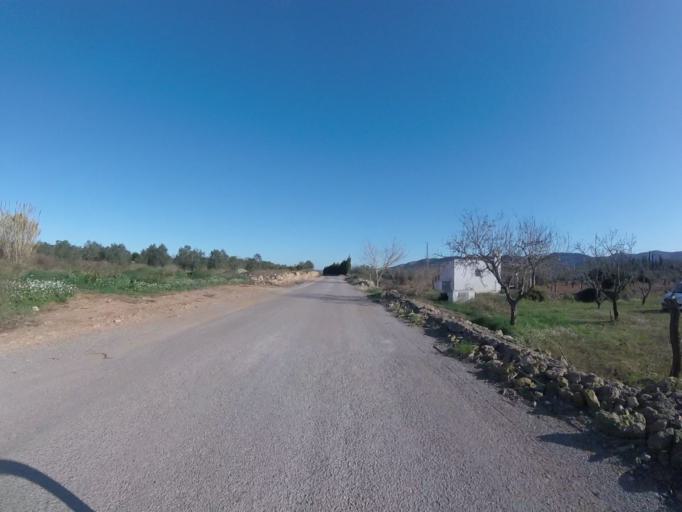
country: ES
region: Valencia
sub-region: Provincia de Castello
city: Alcala de Xivert
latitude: 40.2885
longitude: 0.2149
